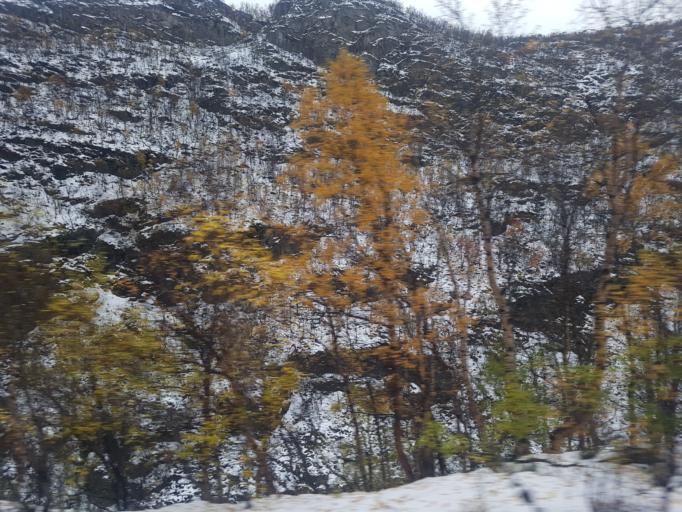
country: NO
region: Sor-Trondelag
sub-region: Oppdal
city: Oppdal
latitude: 62.3634
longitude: 9.6337
